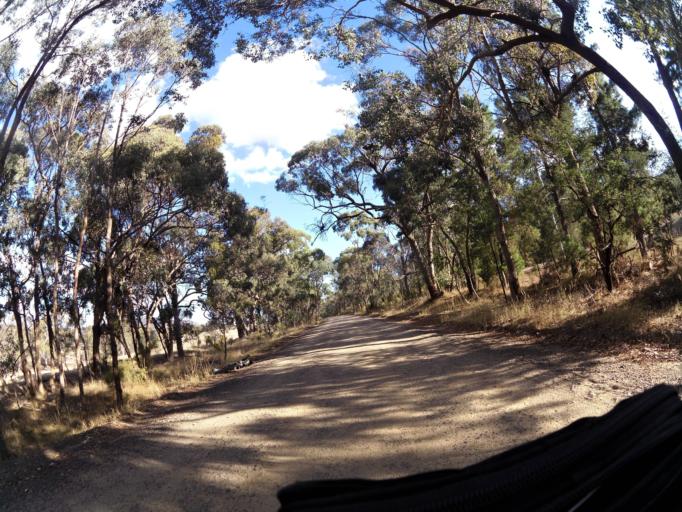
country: AU
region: Victoria
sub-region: Greater Bendigo
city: Kennington
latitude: -37.0139
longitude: 144.8082
